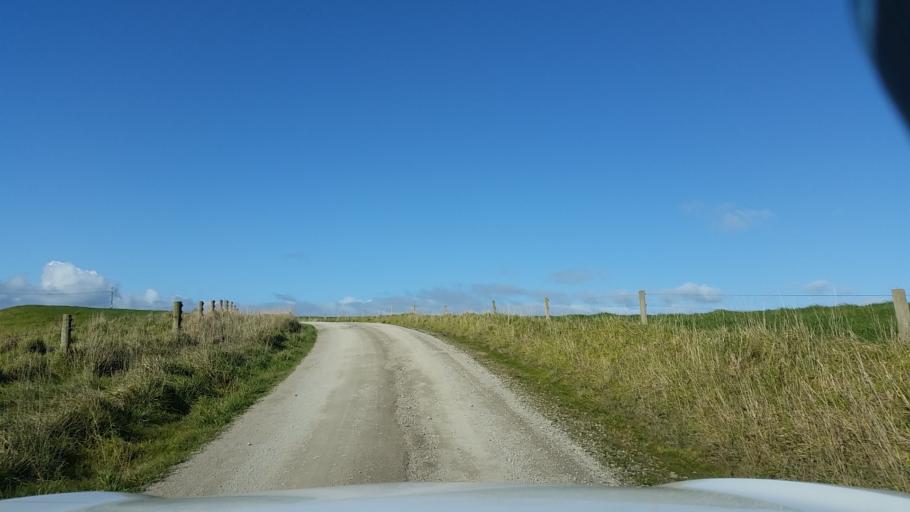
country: NZ
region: Taranaki
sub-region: South Taranaki District
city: Patea
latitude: -39.6844
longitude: 174.3921
